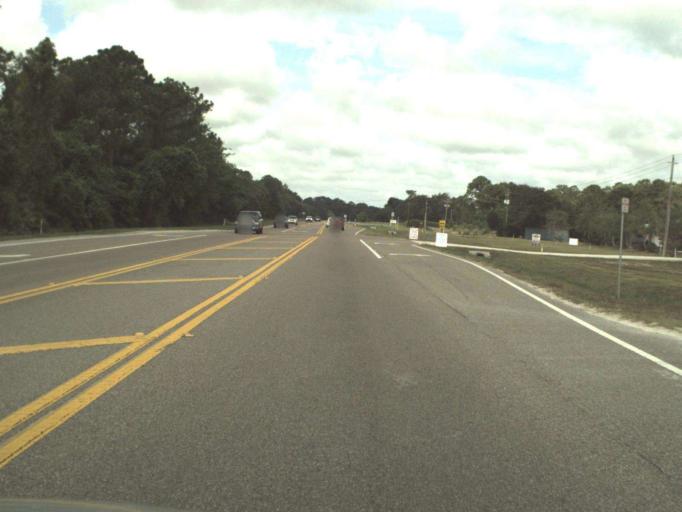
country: US
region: Florida
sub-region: Seminole County
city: Heathrow
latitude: 28.8127
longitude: -81.3781
